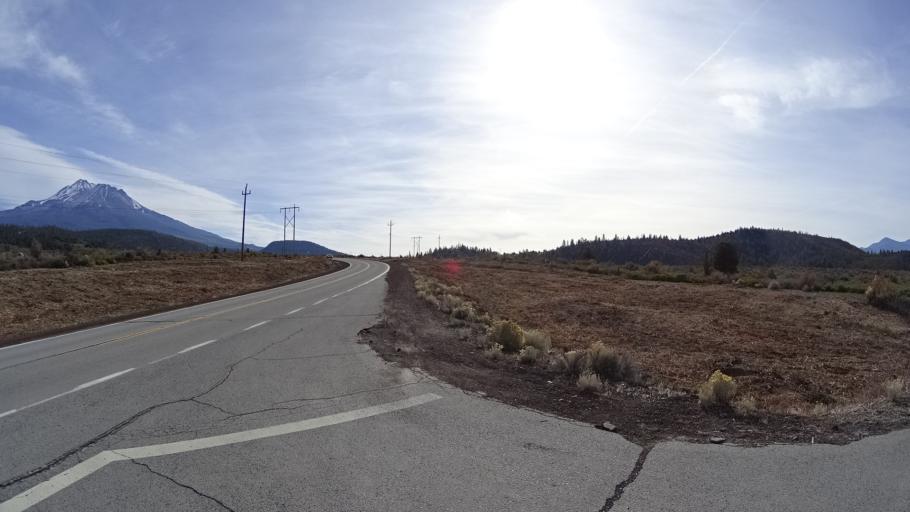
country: US
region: California
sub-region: Siskiyou County
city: Weed
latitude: 41.4813
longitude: -122.3625
